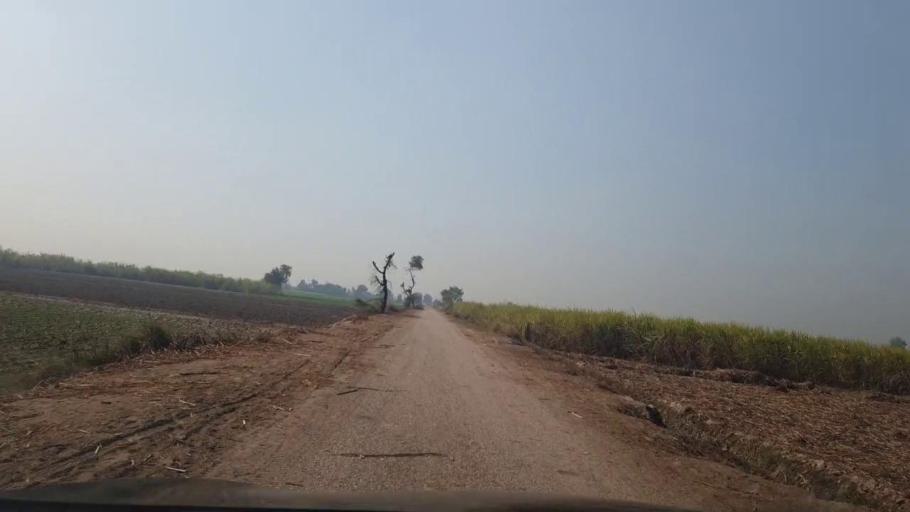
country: PK
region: Sindh
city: Ubauro
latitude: 28.1234
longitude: 69.8172
